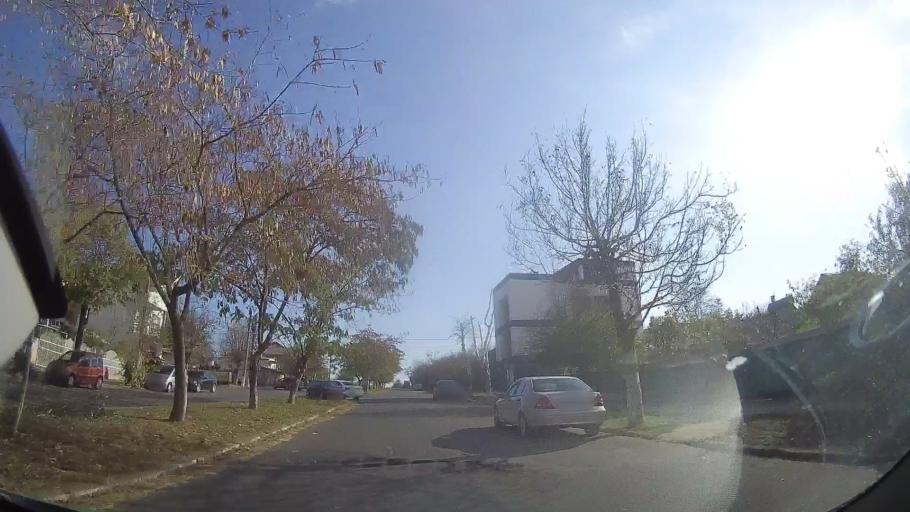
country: RO
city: Eforie Sud
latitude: 44.0208
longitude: 28.6481
